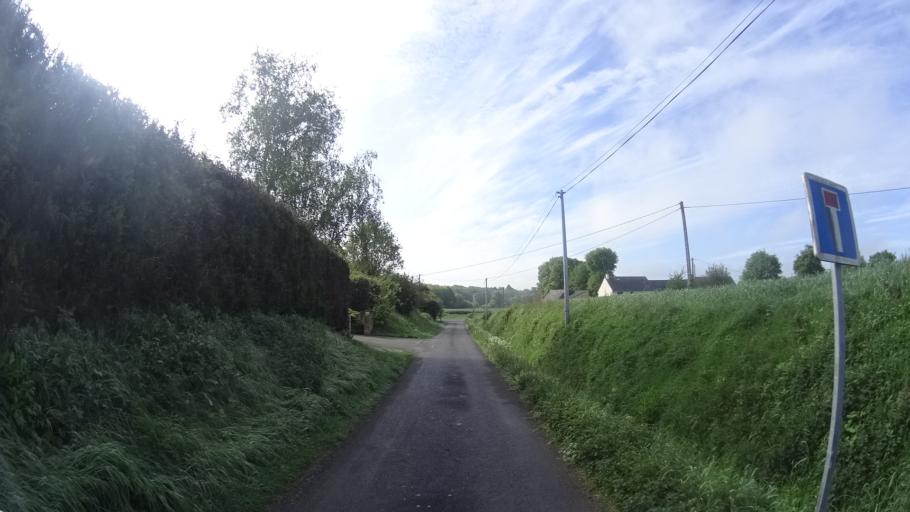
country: FR
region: Brittany
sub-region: Departement d'Ille-et-Vilaine
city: Mordelles
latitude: 48.0809
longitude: -1.8278
